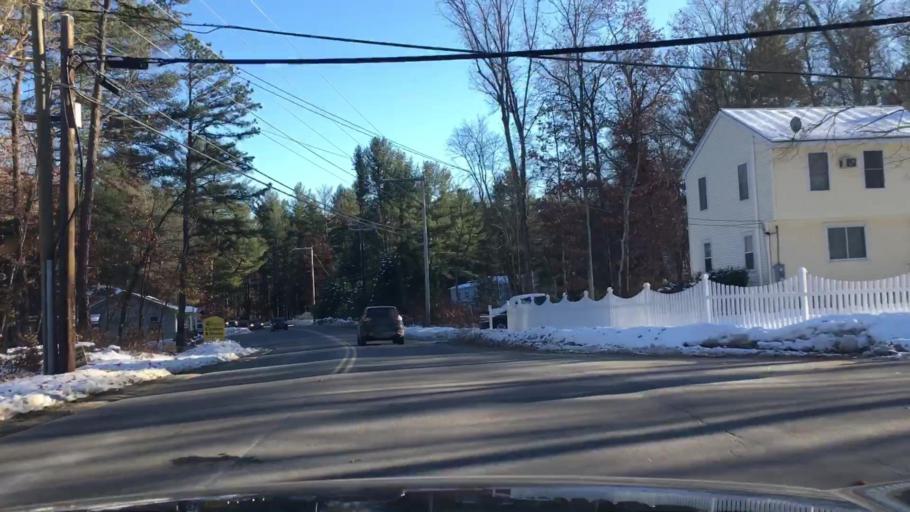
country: US
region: New Hampshire
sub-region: Hillsborough County
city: Milford
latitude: 42.8204
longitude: -71.5811
